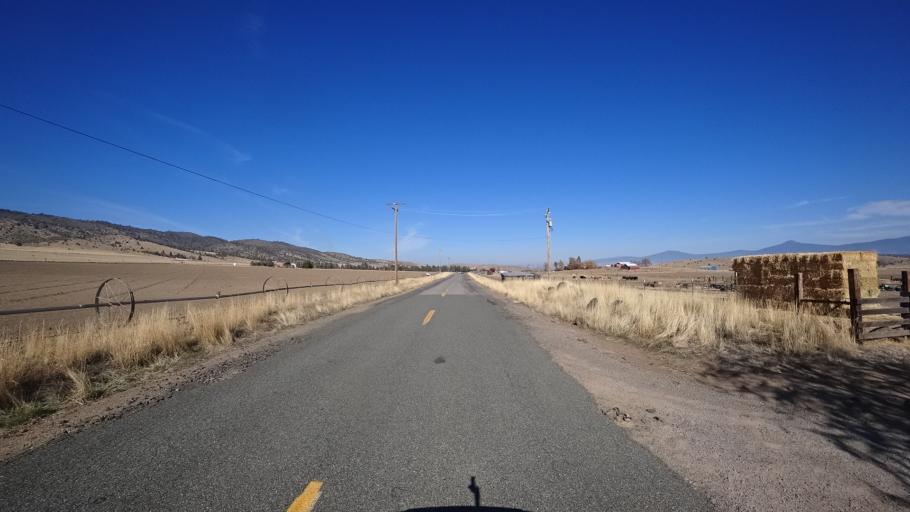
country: US
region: California
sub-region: Siskiyou County
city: Montague
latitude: 41.5760
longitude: -122.5473
